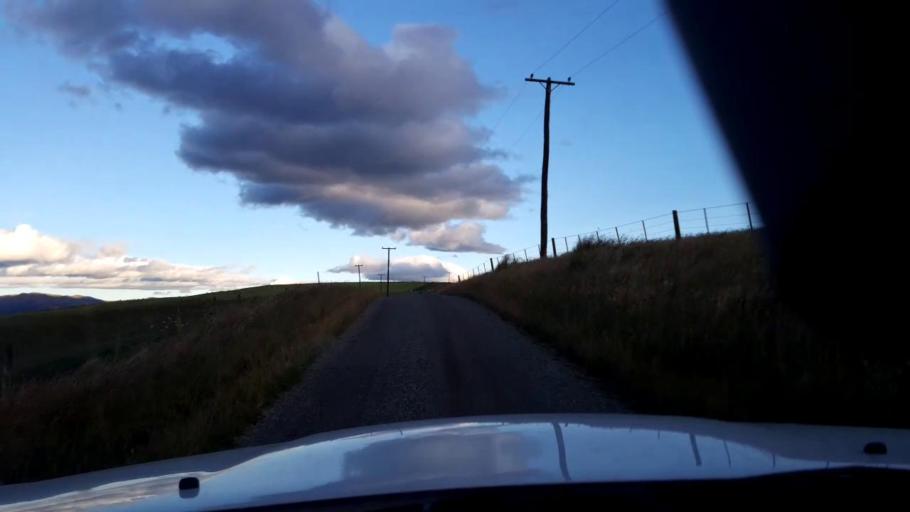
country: NZ
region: Canterbury
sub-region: Timaru District
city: Pleasant Point
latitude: -44.2532
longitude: 170.9110
